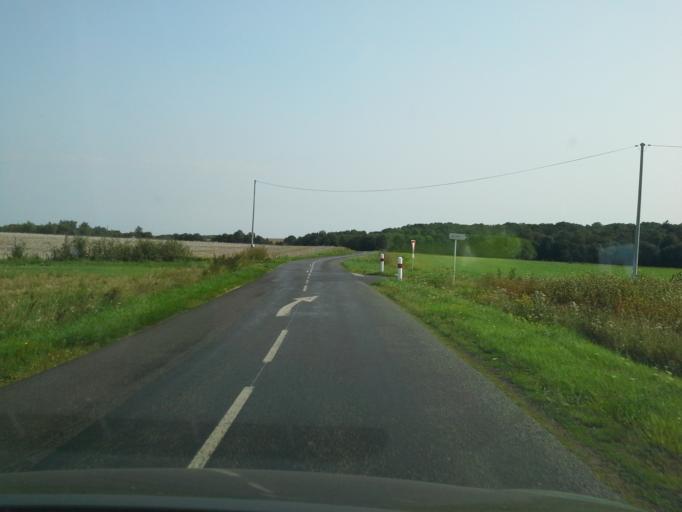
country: FR
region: Centre
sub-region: Departement du Loir-et-Cher
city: La Ville-aux-Clercs
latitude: 47.9031
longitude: 1.0423
